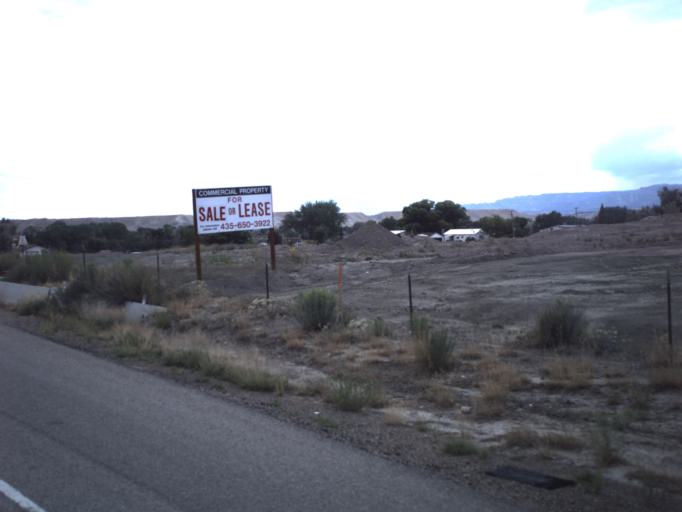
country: US
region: Utah
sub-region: Carbon County
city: Price
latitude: 39.5735
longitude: -110.8161
